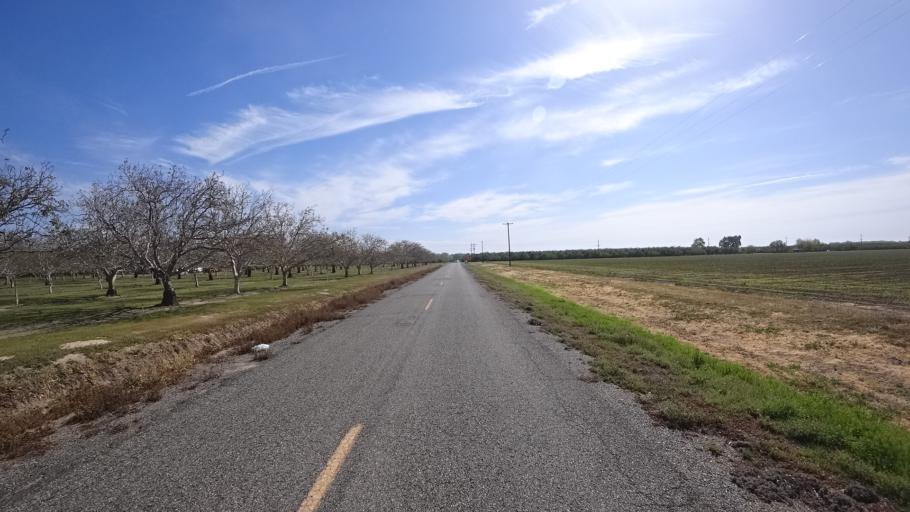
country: US
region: California
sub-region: Glenn County
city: Hamilton City
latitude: 39.6160
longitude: -122.0106
